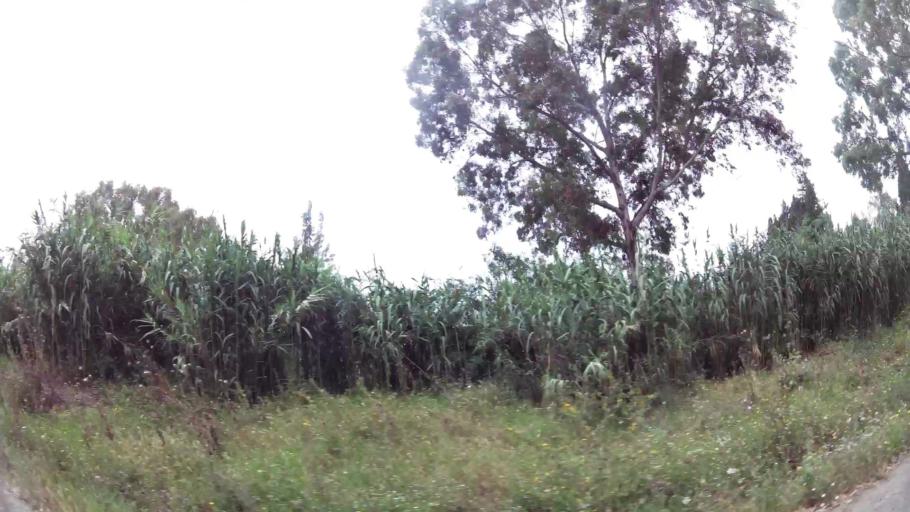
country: MA
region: Rabat-Sale-Zemmour-Zaer
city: Sale
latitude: 33.9944
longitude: -6.7694
